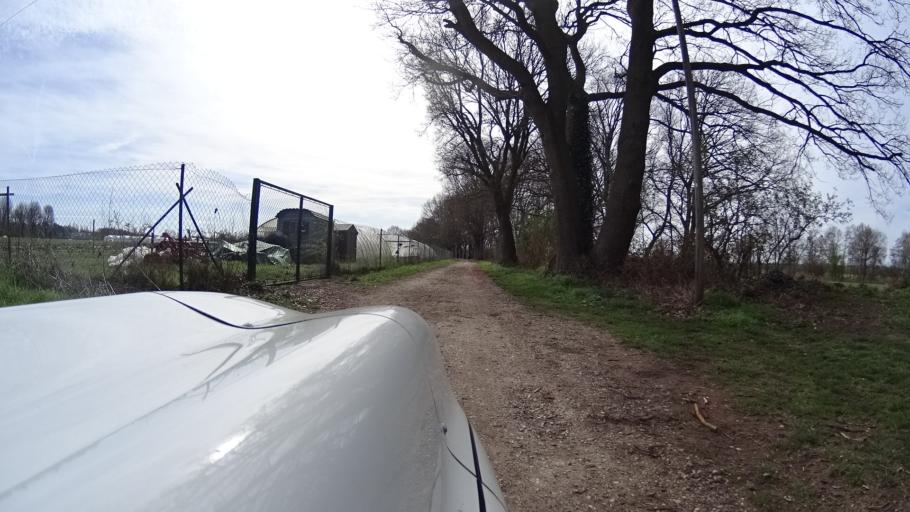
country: DE
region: North Rhine-Westphalia
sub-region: Regierungsbezirk Dusseldorf
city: Kevelaer
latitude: 51.5997
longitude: 6.2481
